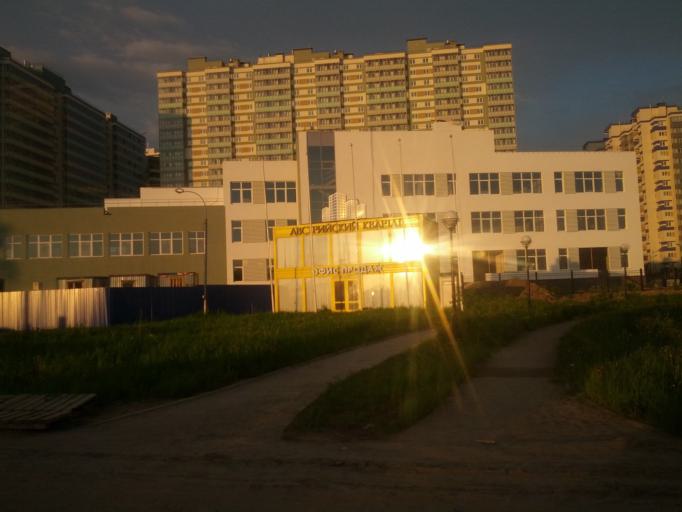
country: RU
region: Leningrad
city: Rybatskoye
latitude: 59.9026
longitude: 30.5057
